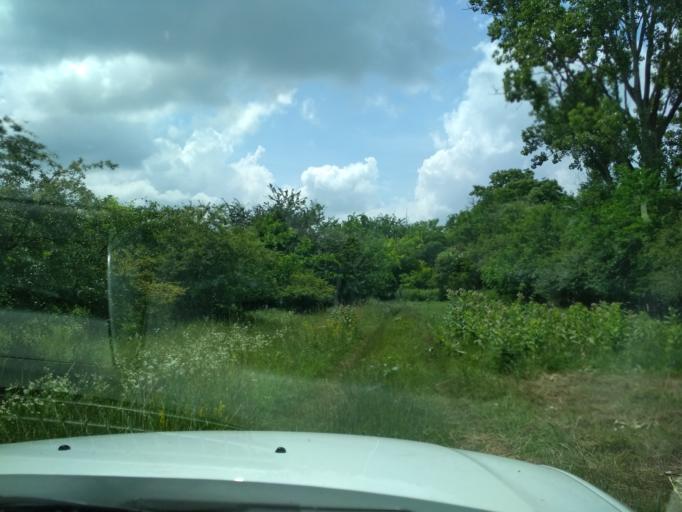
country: HU
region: Pest
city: Tapiosag
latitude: 47.4120
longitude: 19.6499
